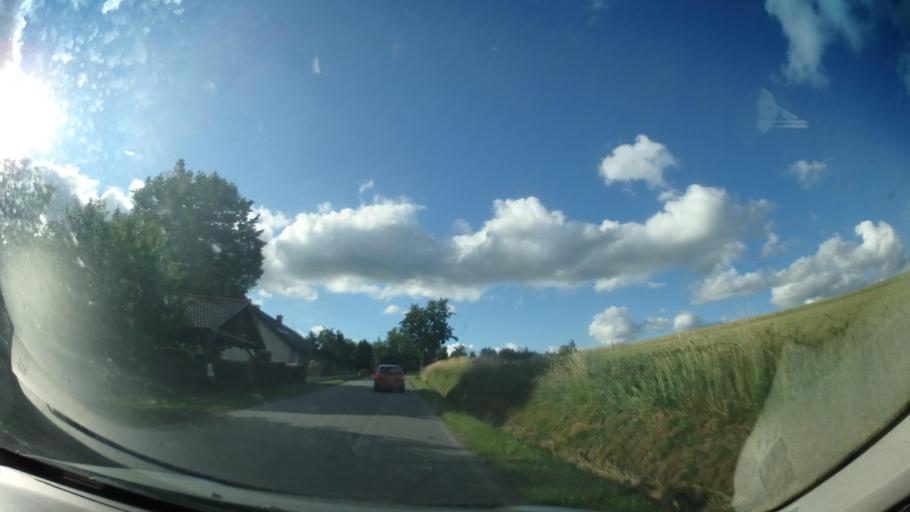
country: CZ
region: Vysocina
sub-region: Okres Zd'ar nad Sazavou
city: Jimramov
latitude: 49.5826
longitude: 16.1872
